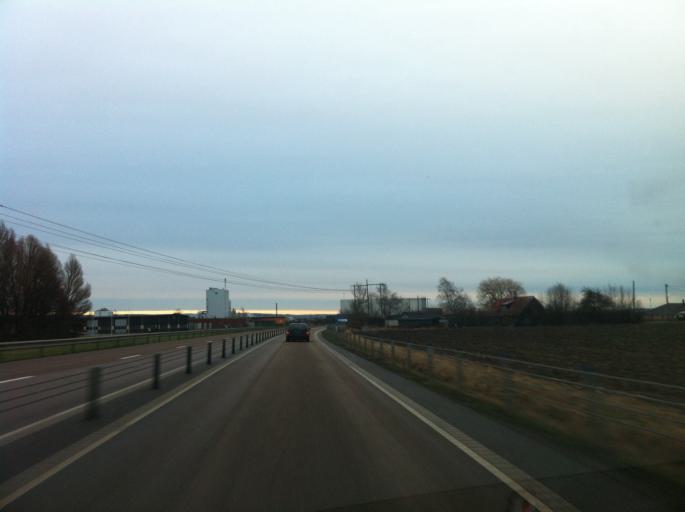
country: SE
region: Skane
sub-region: Bjuvs Kommun
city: Bjuv
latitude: 56.0737
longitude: 12.9256
